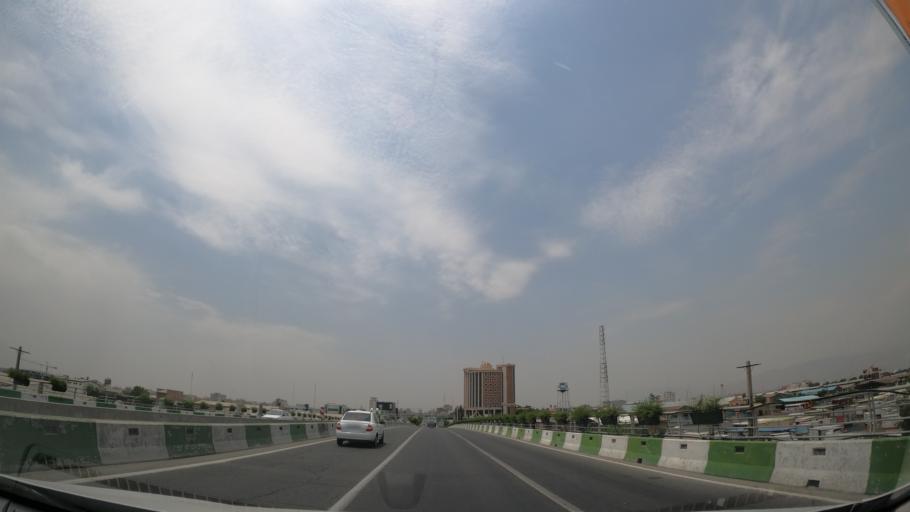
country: IR
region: Tehran
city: Tehran
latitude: 35.6757
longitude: 51.3085
